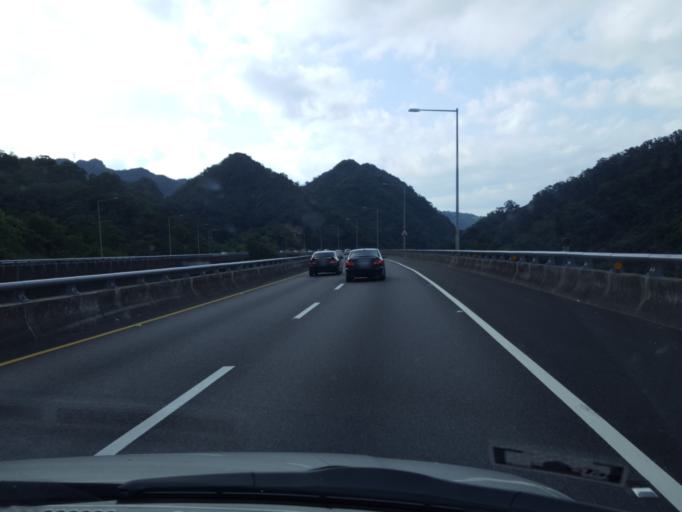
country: TW
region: Taipei
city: Taipei
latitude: 24.9807
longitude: 121.6736
